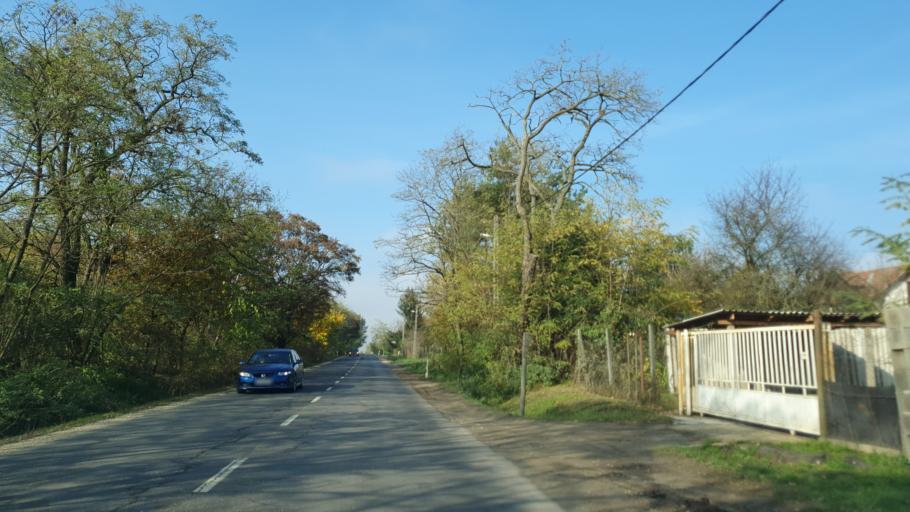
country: HU
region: Pest
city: Szod
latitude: 47.7399
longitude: 19.1875
